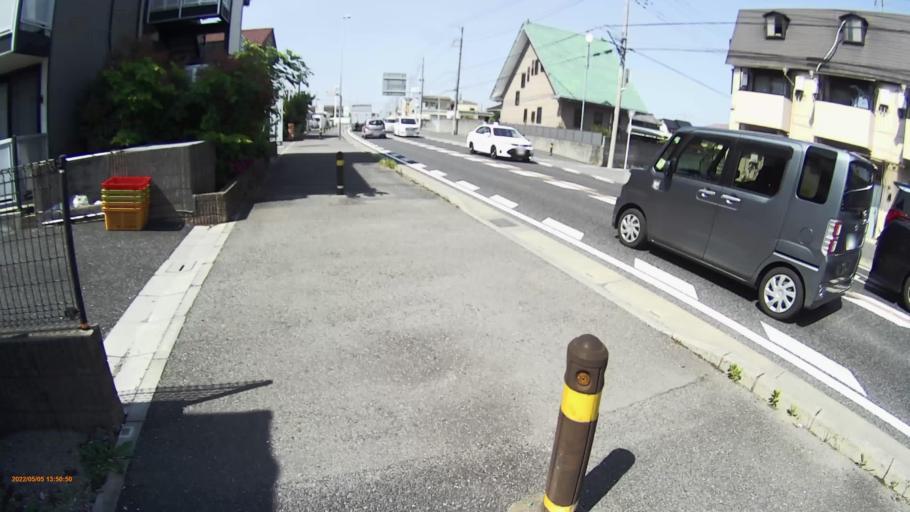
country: JP
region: Saitama
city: Kasukabe
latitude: 35.9945
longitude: 139.7523
